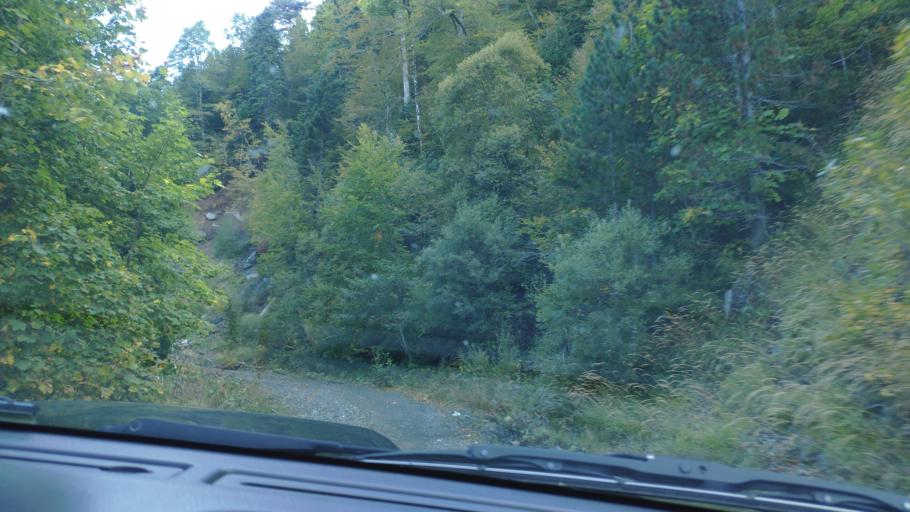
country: AL
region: Korce
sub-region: Rrethi i Devollit
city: Miras
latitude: 40.3397
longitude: 20.8955
